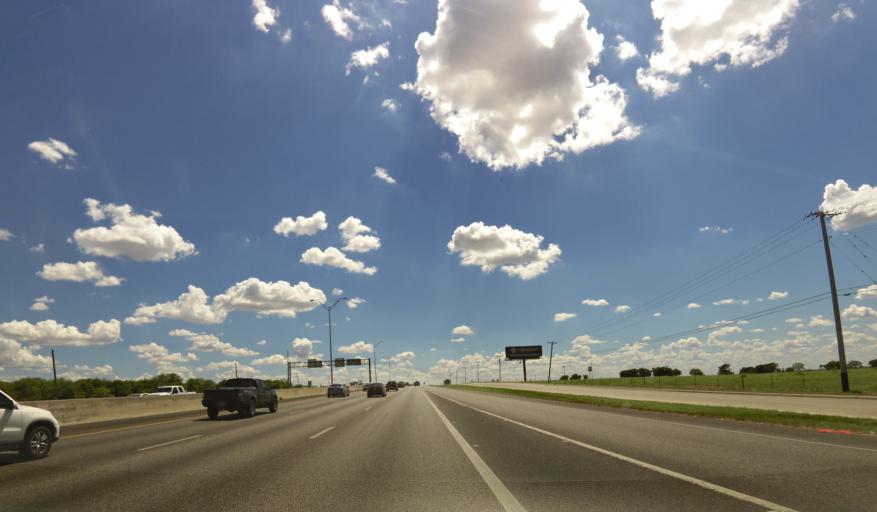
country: US
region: Texas
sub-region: Guadalupe County
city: Northcliff
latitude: 29.6386
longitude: -98.2144
